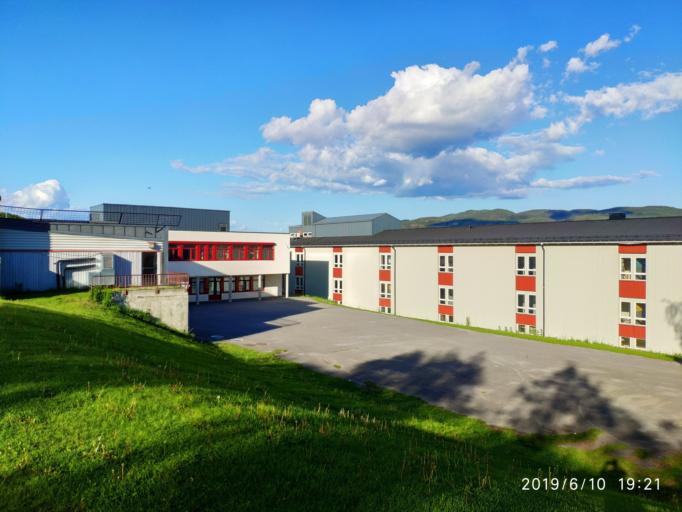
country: NO
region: Oppland
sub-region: Jevnaker
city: Jevnaker
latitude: 60.2395
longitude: 10.3657
